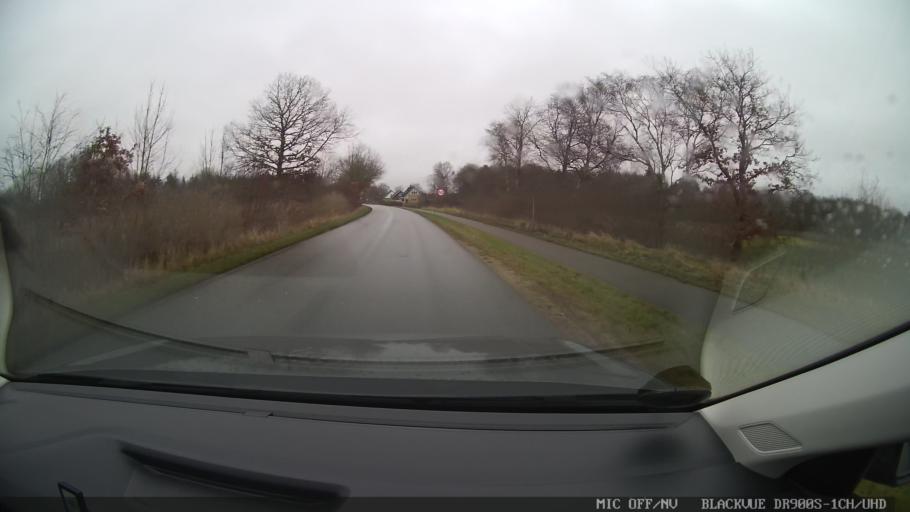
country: DK
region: Central Jutland
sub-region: Viborg Kommune
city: Karup
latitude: 56.2959
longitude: 9.1451
